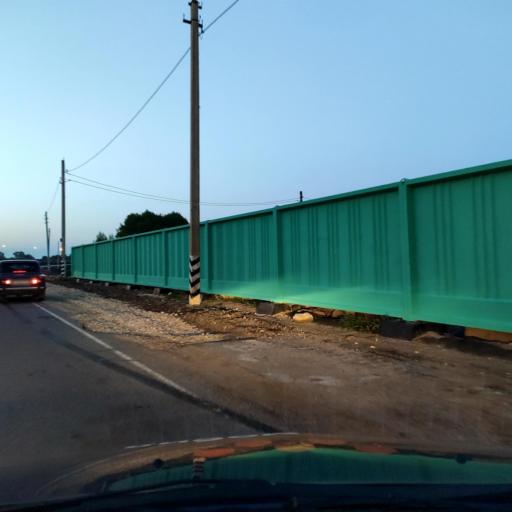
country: RU
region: Orjol
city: Zmiyevka
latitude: 52.7039
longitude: 36.3682
